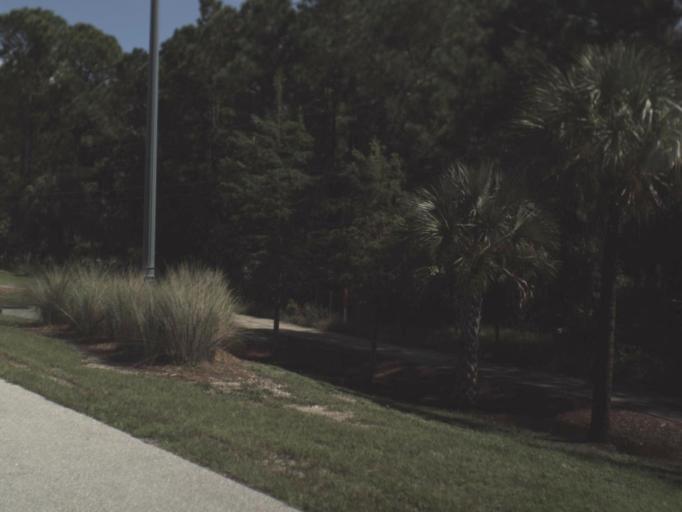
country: US
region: Florida
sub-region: Sarasota County
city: North Port
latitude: 27.0721
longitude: -82.1560
